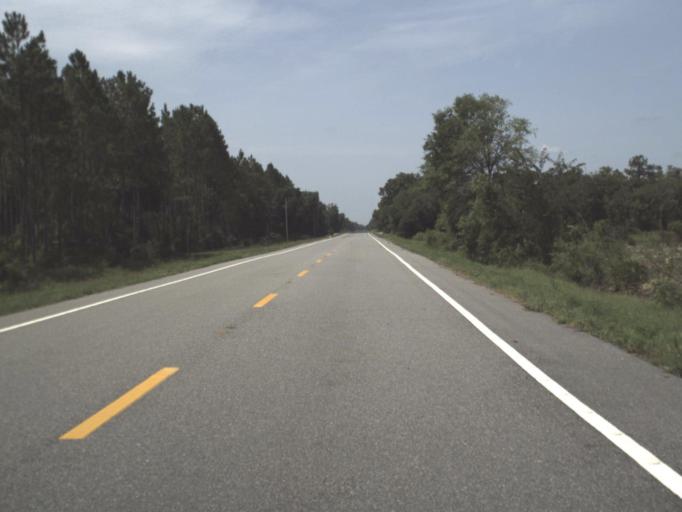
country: US
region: Florida
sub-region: Taylor County
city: Steinhatchee
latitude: 29.8140
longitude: -83.3172
